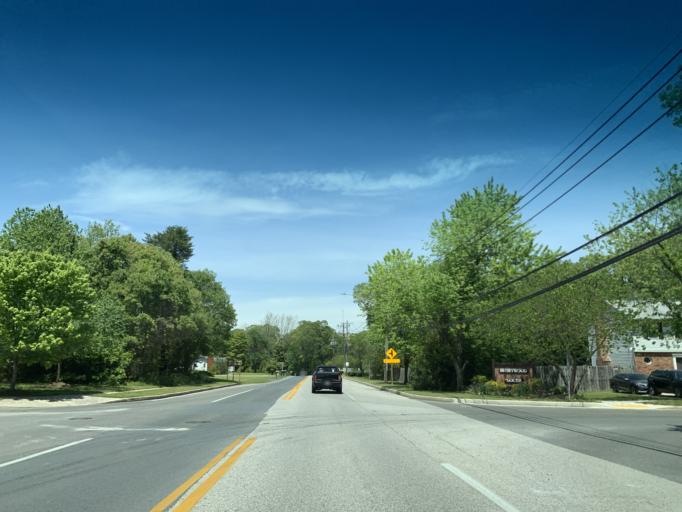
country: US
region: Maryland
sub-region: Anne Arundel County
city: Severna Park
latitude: 39.0836
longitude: -76.5482
